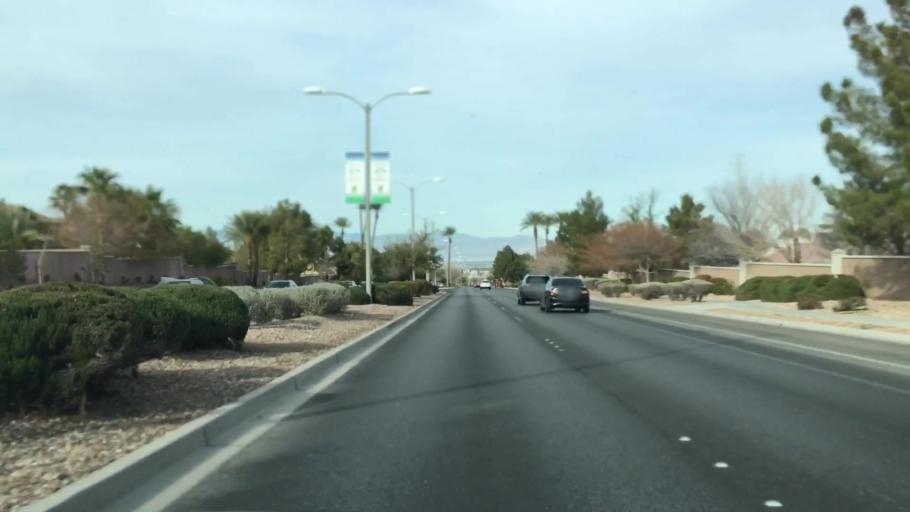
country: US
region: Nevada
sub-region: Clark County
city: Whitney
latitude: 36.0111
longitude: -115.0831
